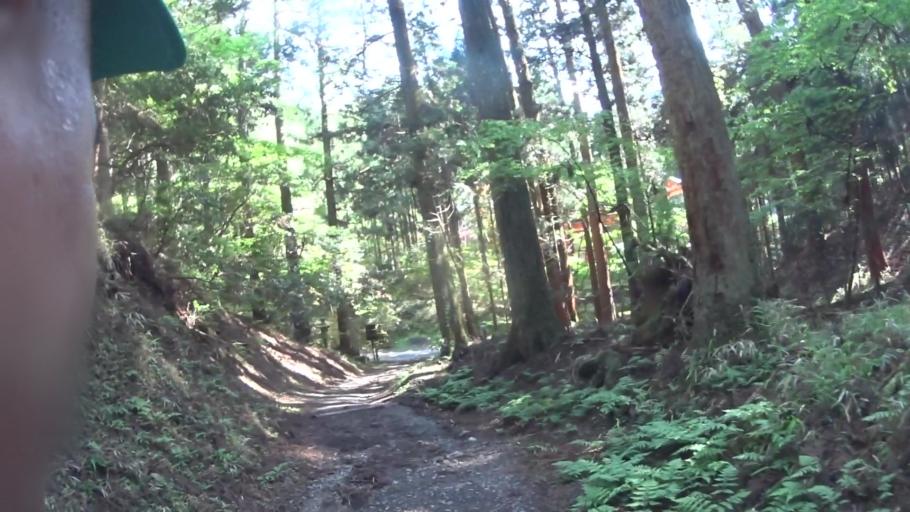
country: JP
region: Shiga Prefecture
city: Otsu-shi
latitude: 35.0974
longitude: 135.8503
